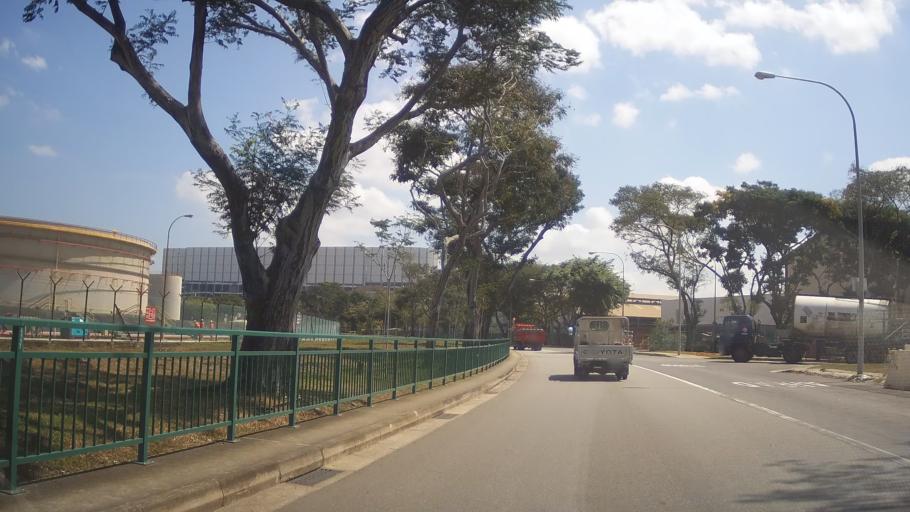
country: SG
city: Singapore
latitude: 1.3039
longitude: 103.6911
